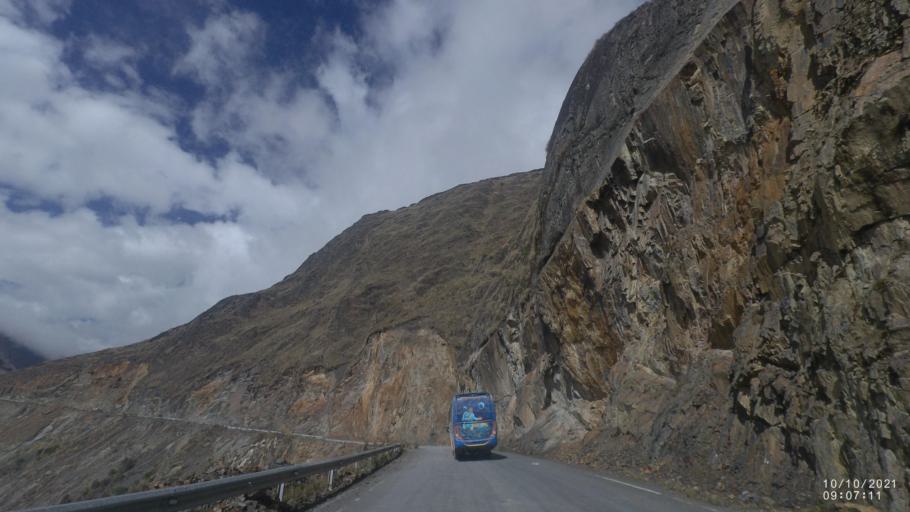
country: BO
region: La Paz
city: Quime
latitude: -17.0086
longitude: -67.2746
